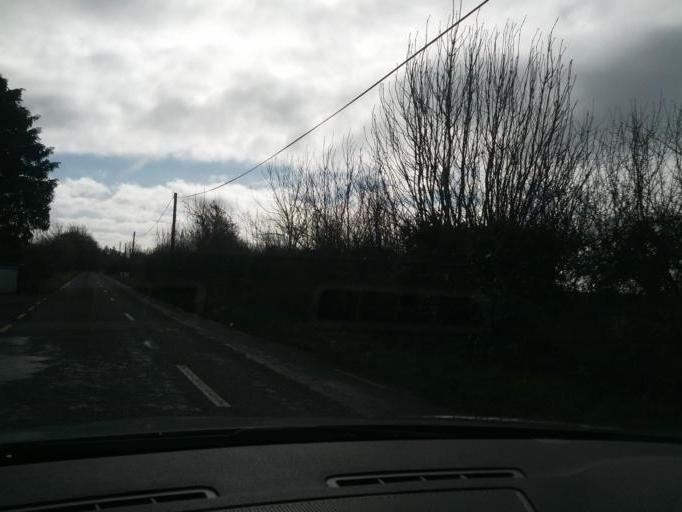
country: IE
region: Connaught
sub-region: County Galway
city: Ballinasloe
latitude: 53.4293
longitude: -8.4181
